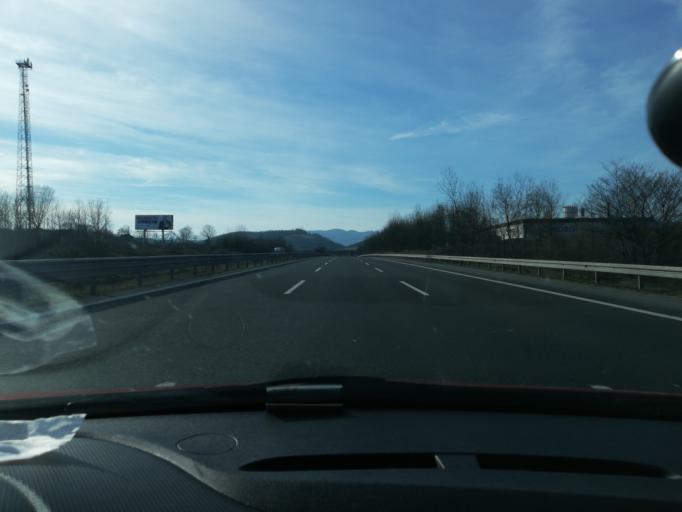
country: TR
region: Duzce
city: Gumusova
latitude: 40.8402
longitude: 30.9839
